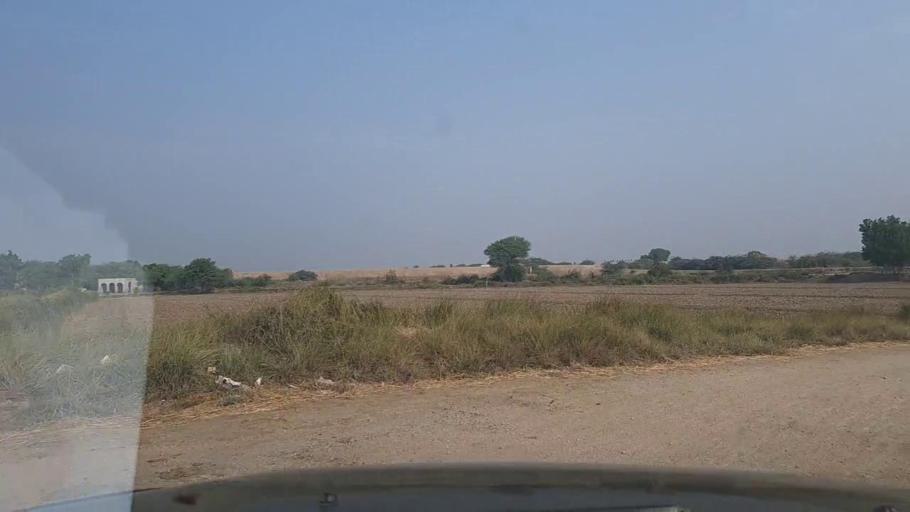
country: PK
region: Sindh
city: Bulri
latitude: 24.9414
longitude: 68.2803
